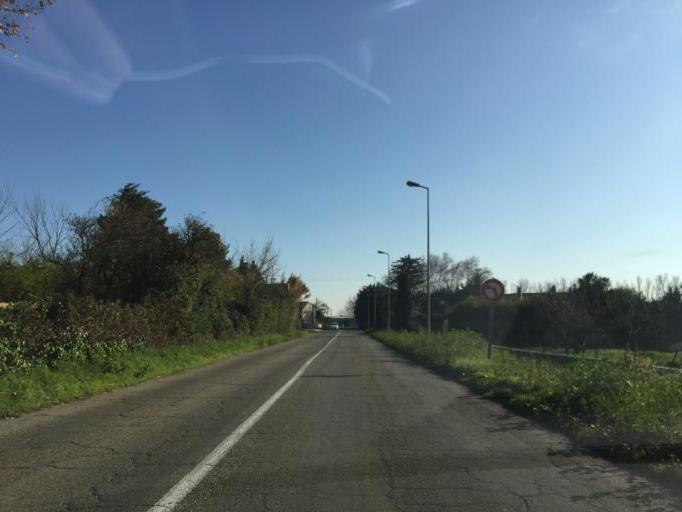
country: FR
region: Provence-Alpes-Cote d'Azur
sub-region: Departement du Vaucluse
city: Jonquieres
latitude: 44.1144
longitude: 4.9068
